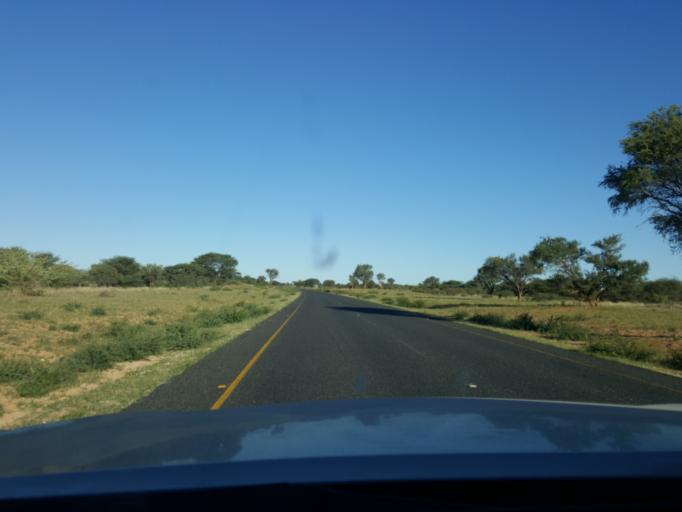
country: BW
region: Southern
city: Khakhea
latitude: -24.2207
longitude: 23.2323
